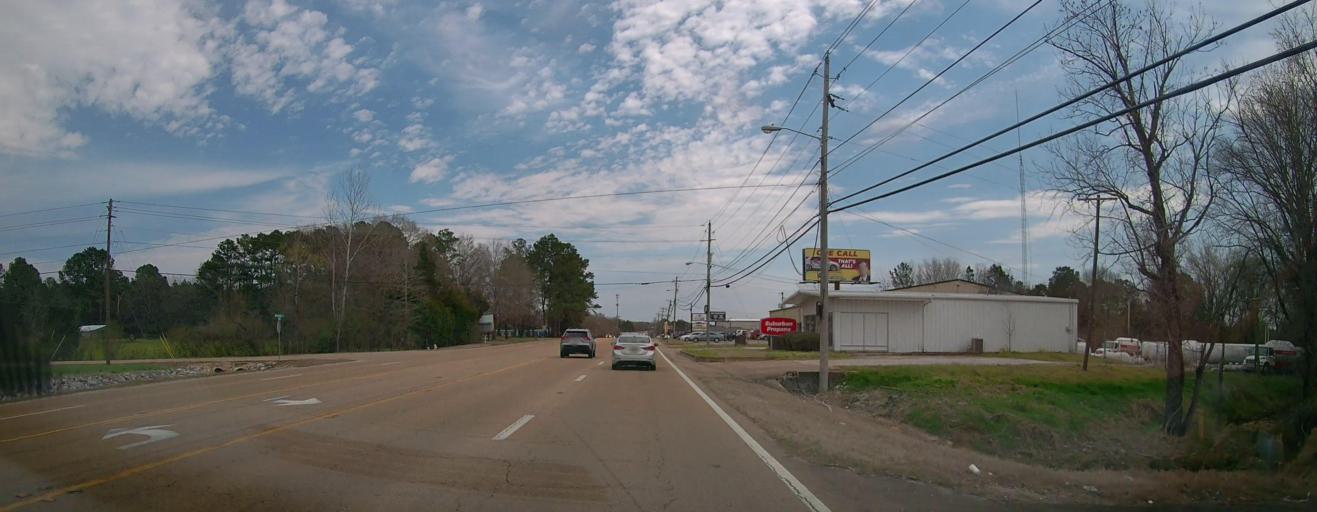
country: US
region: Mississippi
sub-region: Lee County
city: Tupelo
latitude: 34.2926
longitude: -88.7563
